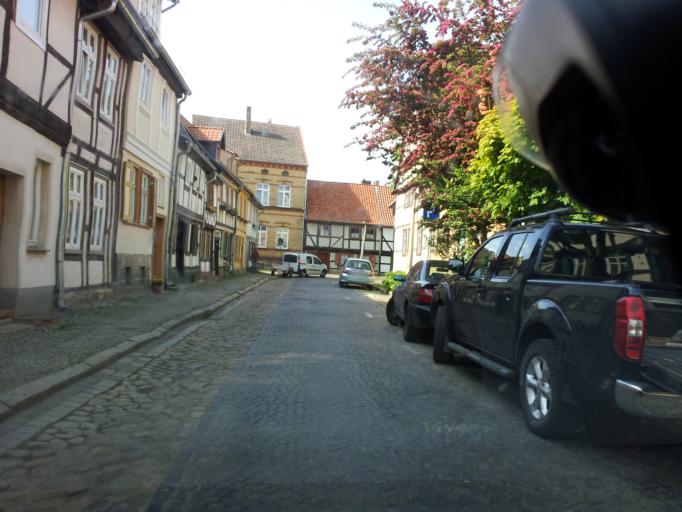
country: DE
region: Saxony-Anhalt
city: Quedlinburg
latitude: 51.7877
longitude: 11.1508
